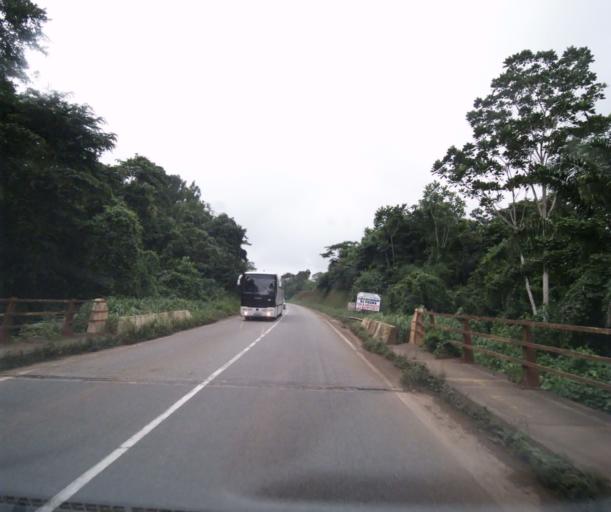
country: CM
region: Centre
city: Eseka
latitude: 3.8732
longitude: 10.6617
